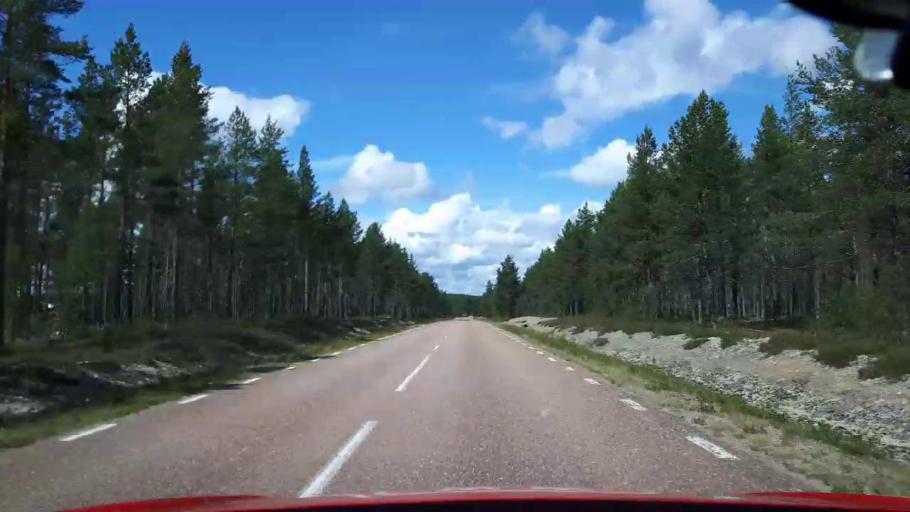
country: SE
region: Dalarna
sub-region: Alvdalens Kommun
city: AElvdalen
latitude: 61.8197
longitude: 13.5779
